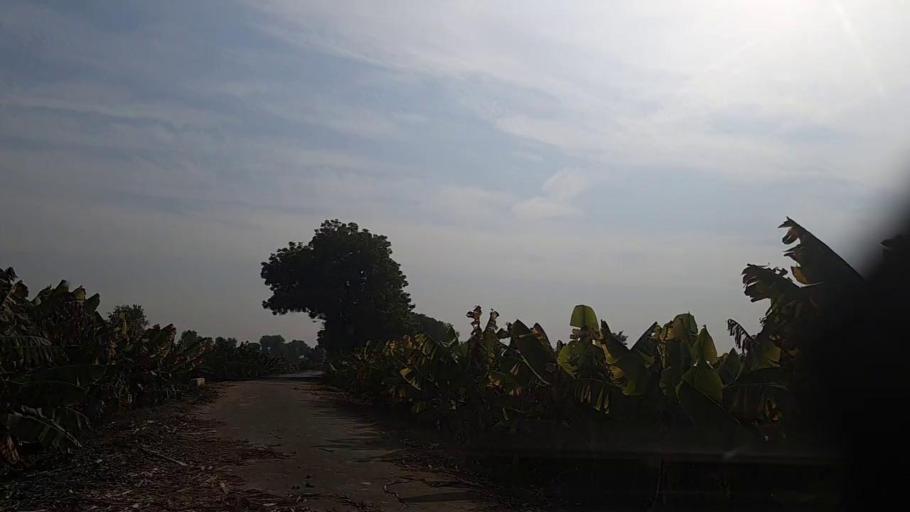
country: PK
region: Sindh
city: Daur
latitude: 26.3964
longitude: 68.2015
